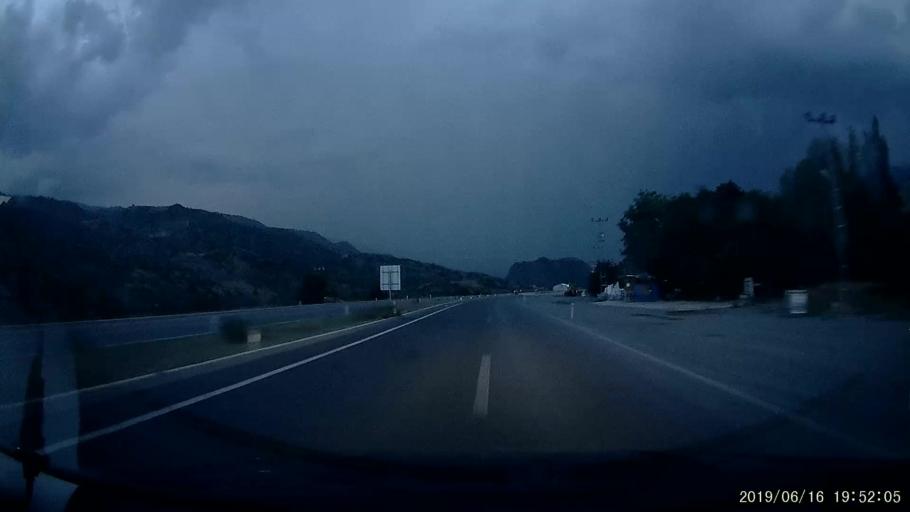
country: TR
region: Sivas
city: Koyulhisar
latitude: 40.2852
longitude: 37.8095
